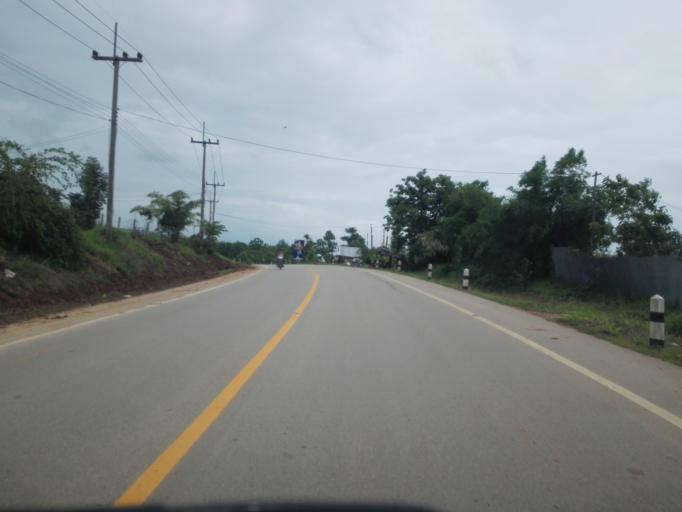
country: TH
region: Tak
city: Mae Sot
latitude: 16.6859
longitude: 98.4703
